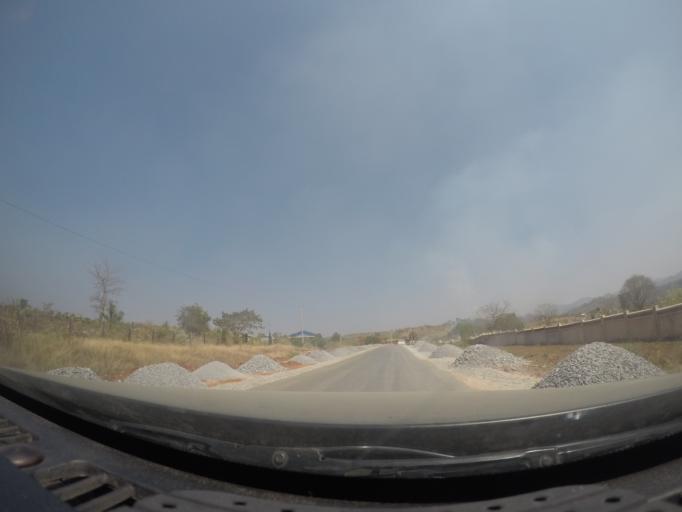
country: MM
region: Shan
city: Taunggyi
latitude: 20.8146
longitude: 97.2089
